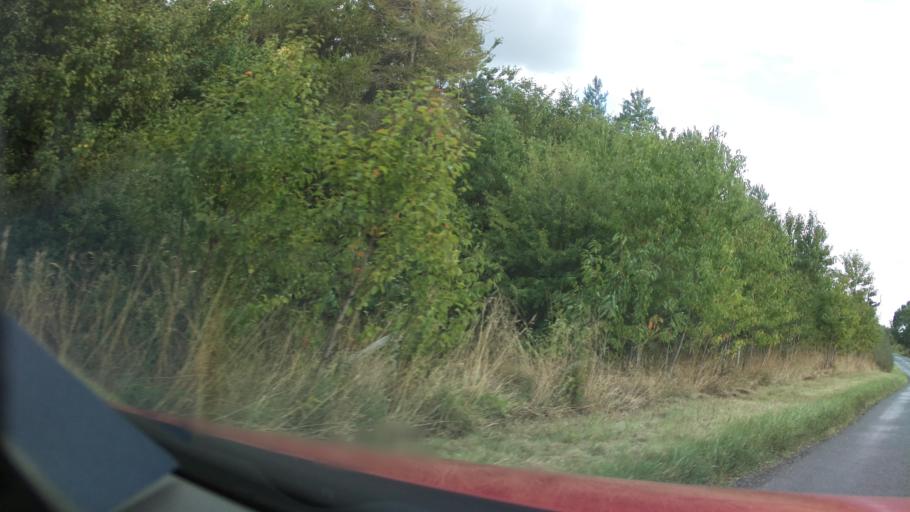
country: GB
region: England
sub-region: North Yorkshire
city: Bedale
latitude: 54.2397
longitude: -1.6826
